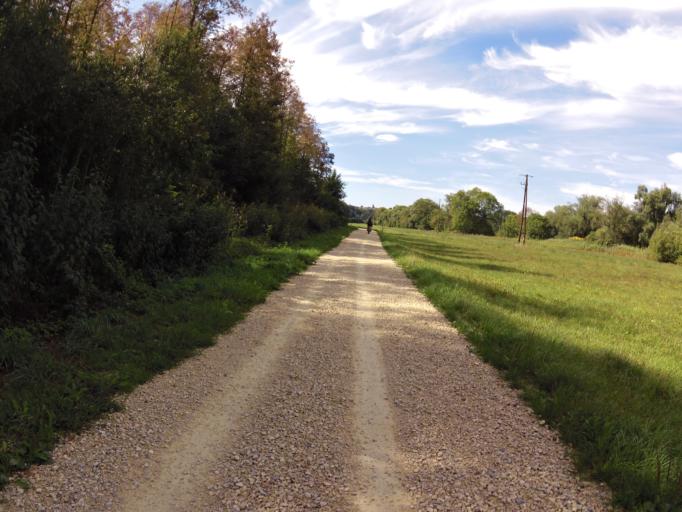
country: DE
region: Baden-Wuerttemberg
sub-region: Regierungsbezirk Stuttgart
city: Neckartailfingen
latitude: 48.6017
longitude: 9.2574
